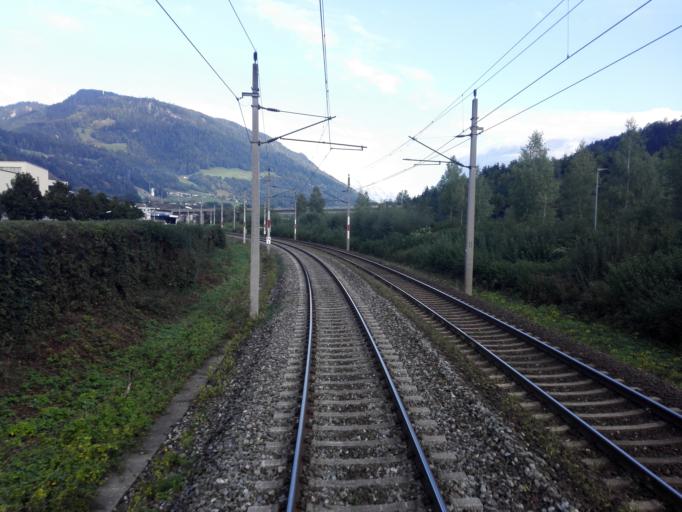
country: AT
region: Salzburg
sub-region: Politischer Bezirk Sankt Johann im Pongau
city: Bischofshofen
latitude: 47.4020
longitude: 13.2243
